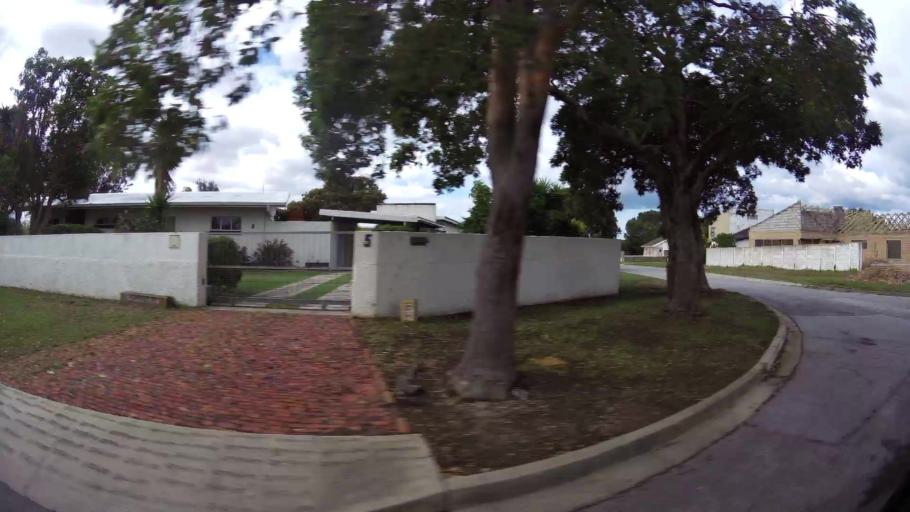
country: ZA
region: Eastern Cape
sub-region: Nelson Mandela Bay Metropolitan Municipality
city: Port Elizabeth
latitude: -33.9338
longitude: 25.5165
